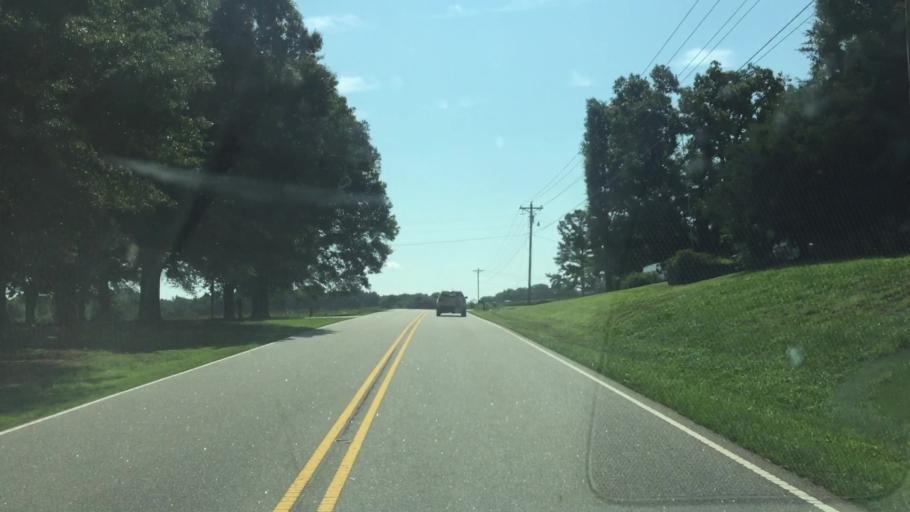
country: US
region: North Carolina
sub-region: Union County
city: Unionville
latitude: 35.1313
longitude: -80.4377
